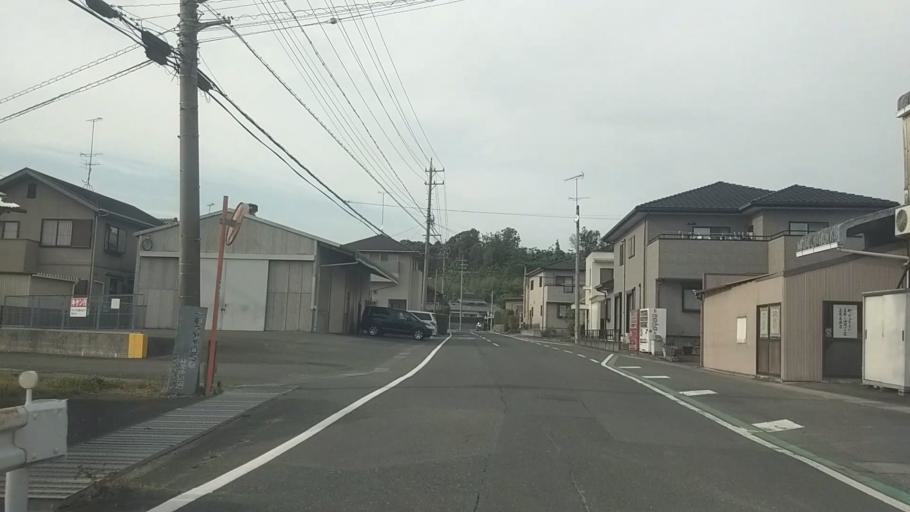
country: JP
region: Shizuoka
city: Kosai-shi
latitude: 34.7432
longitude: 137.6144
